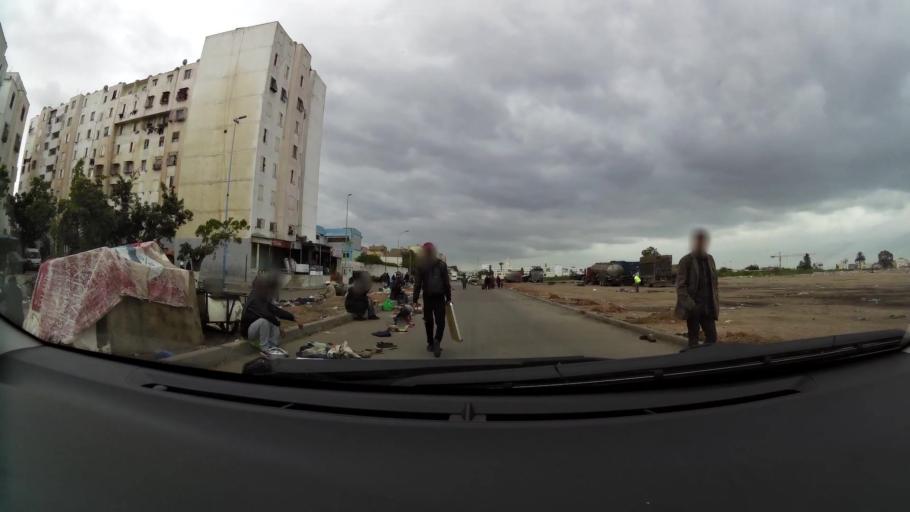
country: MA
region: Grand Casablanca
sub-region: Casablanca
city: Casablanca
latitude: 33.5879
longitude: -7.5576
